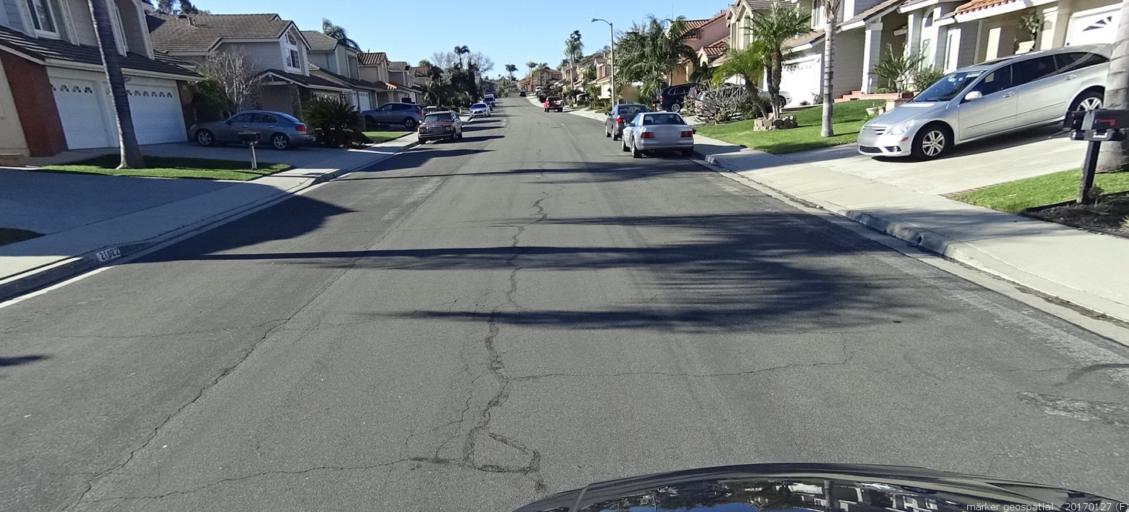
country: US
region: California
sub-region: Orange County
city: Foothill Ranch
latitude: 33.6572
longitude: -117.6607
